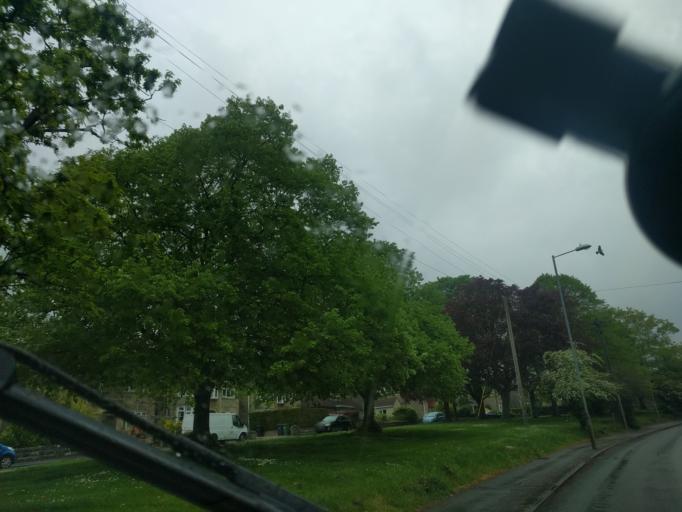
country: GB
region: England
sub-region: Wiltshire
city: Chippenham
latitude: 51.4677
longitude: -2.1231
